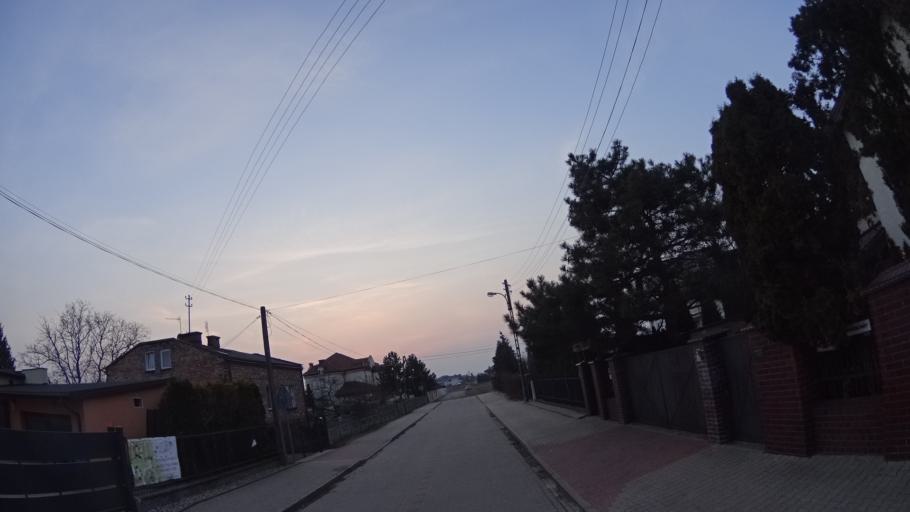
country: PL
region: Masovian Voivodeship
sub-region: Powiat warszawski zachodni
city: Babice
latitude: 52.2452
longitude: 20.8743
